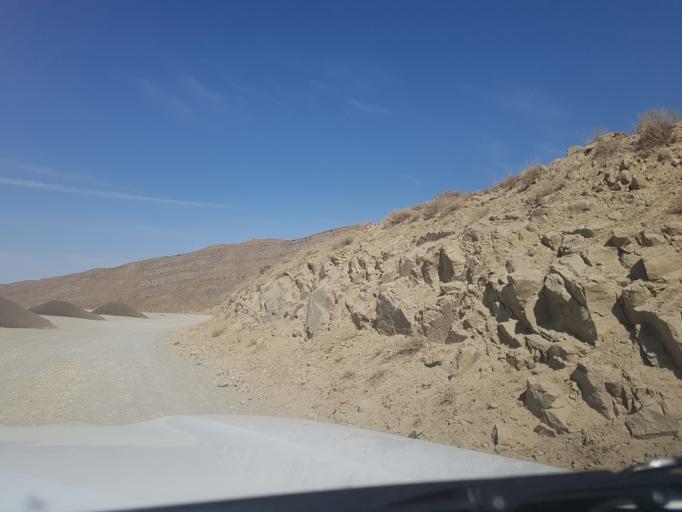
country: TM
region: Ahal
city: Baharly
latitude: 38.4445
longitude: 57.0432
